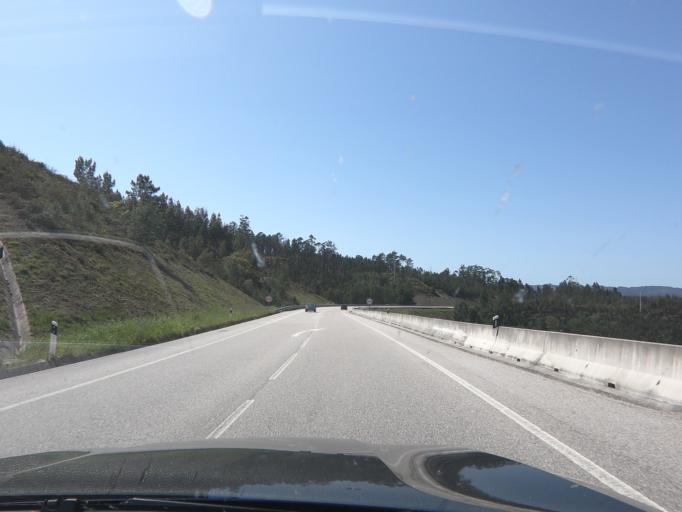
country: PT
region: Coimbra
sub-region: Lousa
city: Lousa
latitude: 40.1498
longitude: -8.2612
